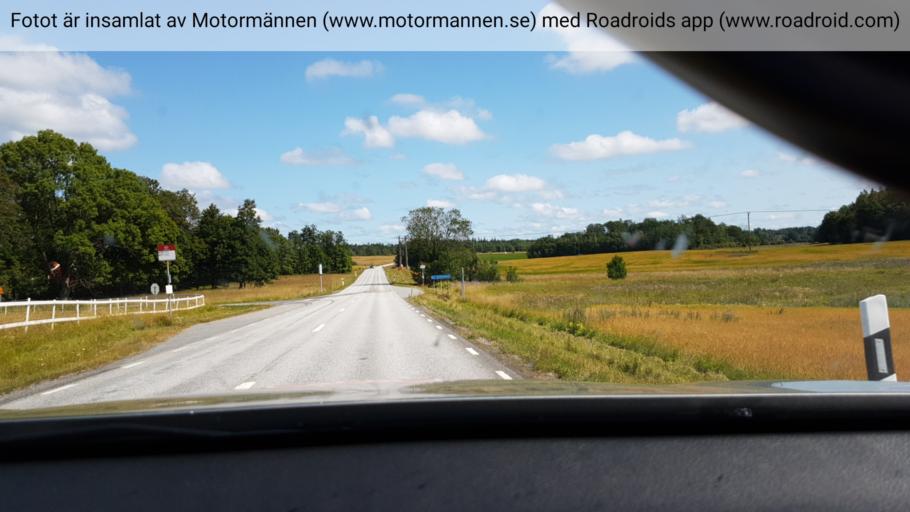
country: SE
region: Stockholm
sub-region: Norrtalje Kommun
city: Hallstavik
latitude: 59.9338
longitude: 18.7157
